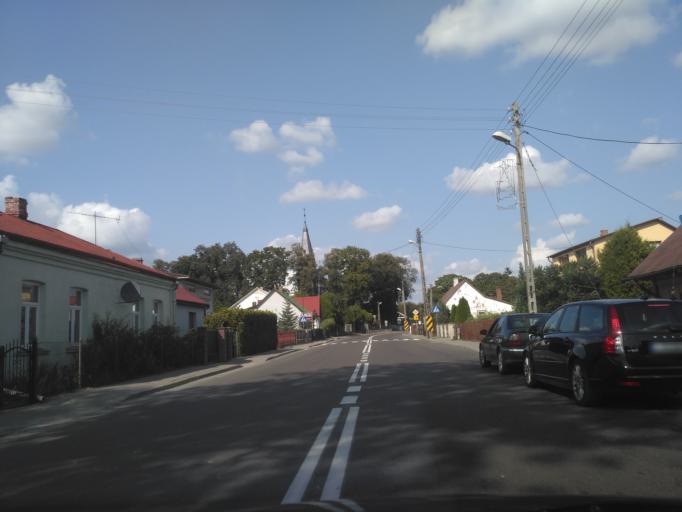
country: PL
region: Lublin Voivodeship
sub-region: Powiat chelmski
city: Rejowiec
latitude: 51.0959
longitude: 23.2843
